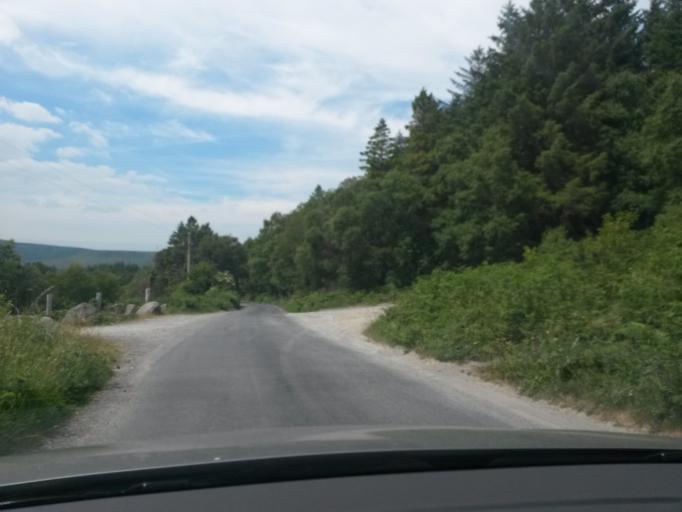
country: IE
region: Leinster
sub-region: Wicklow
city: Enniskerry
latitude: 53.1904
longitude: -6.2436
